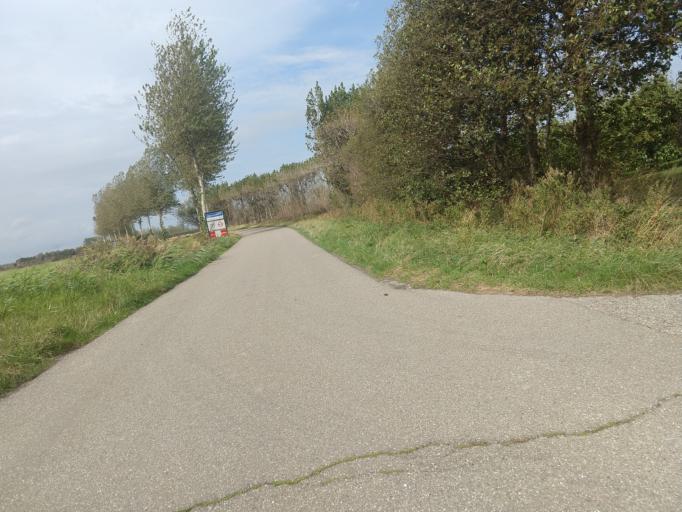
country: NL
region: Zeeland
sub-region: Gemeente Reimerswaal
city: Yerseke
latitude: 51.4528
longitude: 4.0012
